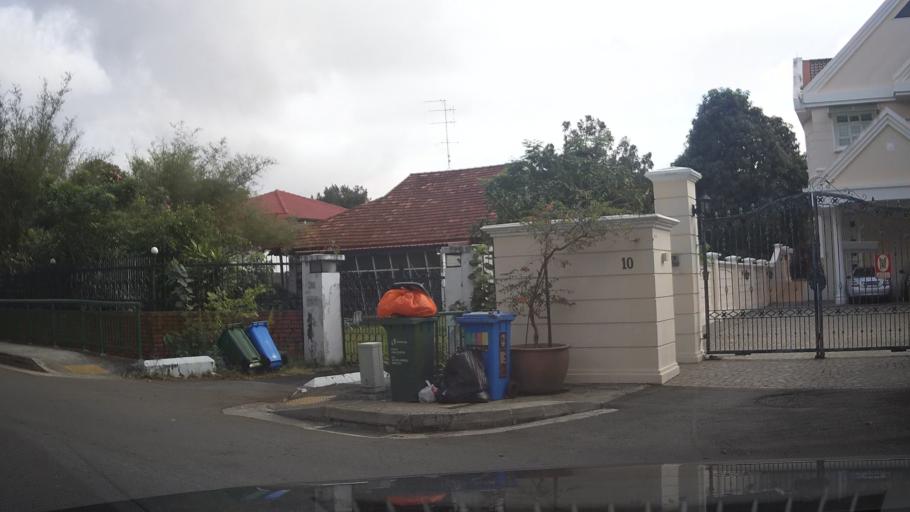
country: SG
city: Singapore
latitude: 1.2990
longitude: 103.8909
